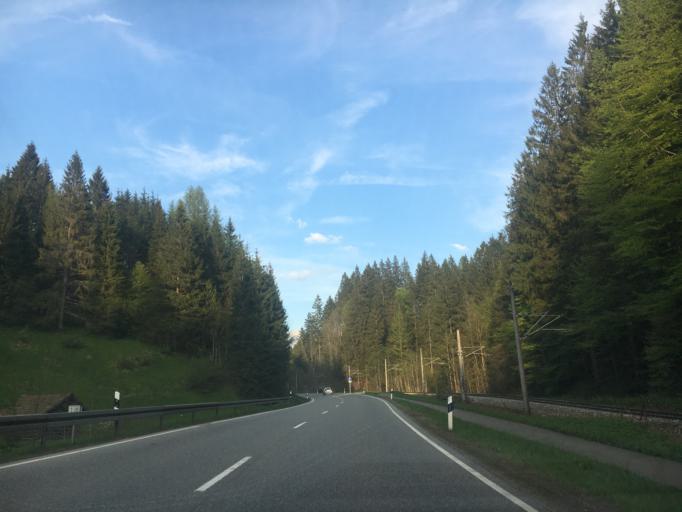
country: DE
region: Bavaria
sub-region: Upper Bavaria
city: Mittenwald
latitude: 47.4885
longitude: 11.1969
